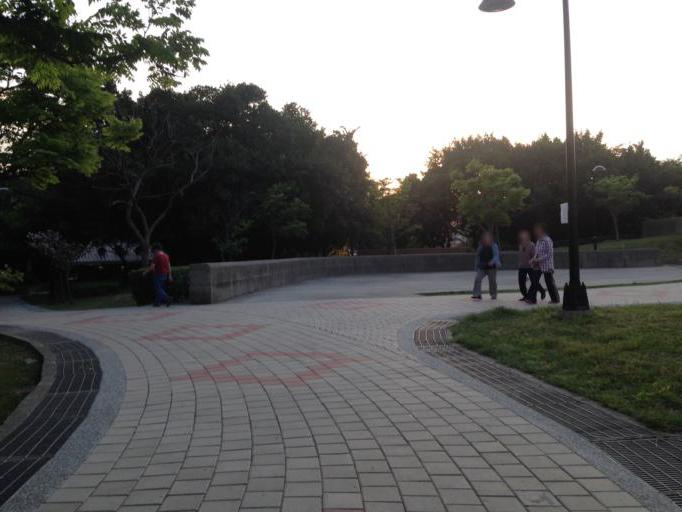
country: TW
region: Taipei
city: Taipei
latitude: 25.1363
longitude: 121.5027
